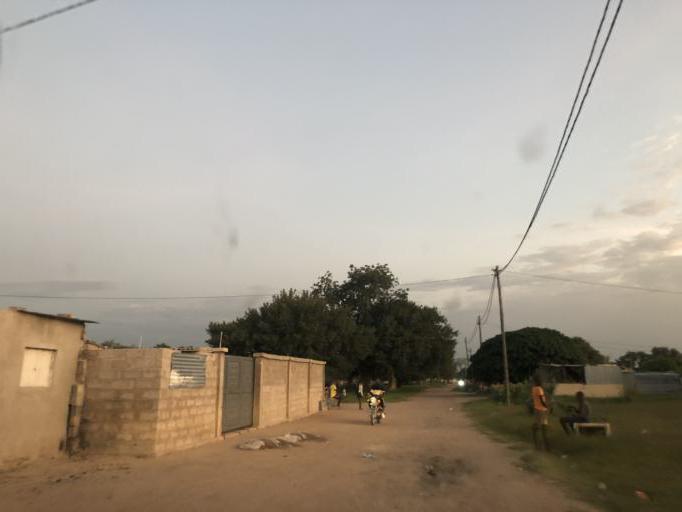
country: AO
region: Cunene
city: Ondjiva
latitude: -17.0625
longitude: 15.7068
